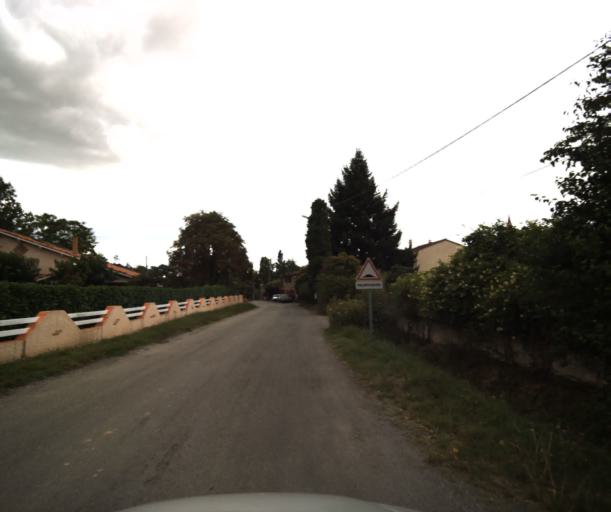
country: FR
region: Midi-Pyrenees
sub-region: Departement de la Haute-Garonne
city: Le Fauga
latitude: 43.4105
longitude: 1.3105
